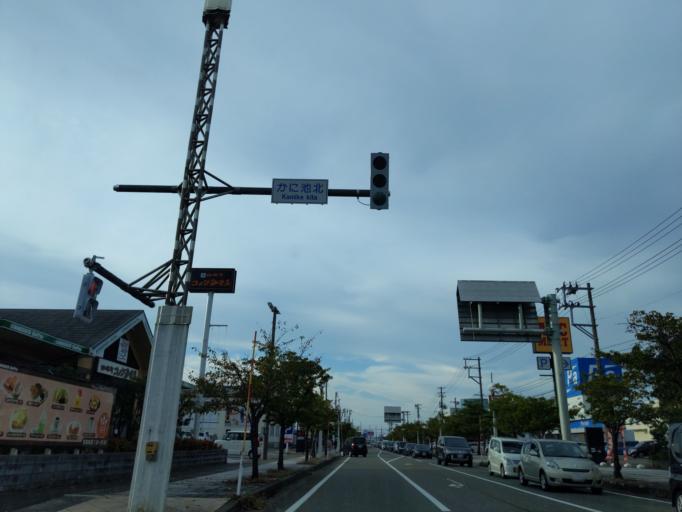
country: JP
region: Niigata
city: Joetsu
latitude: 37.1548
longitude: 138.2548
